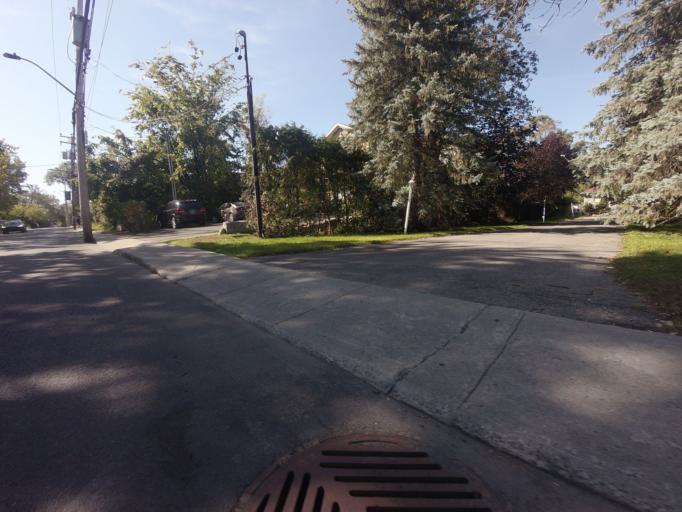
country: CA
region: Quebec
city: Kirkland
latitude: 45.4758
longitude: -73.8744
